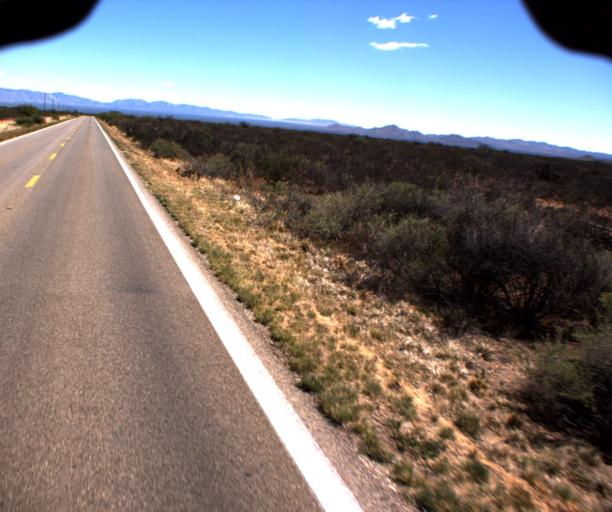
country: US
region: Arizona
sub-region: Cochise County
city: Huachuca City
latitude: 31.7033
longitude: -110.2916
